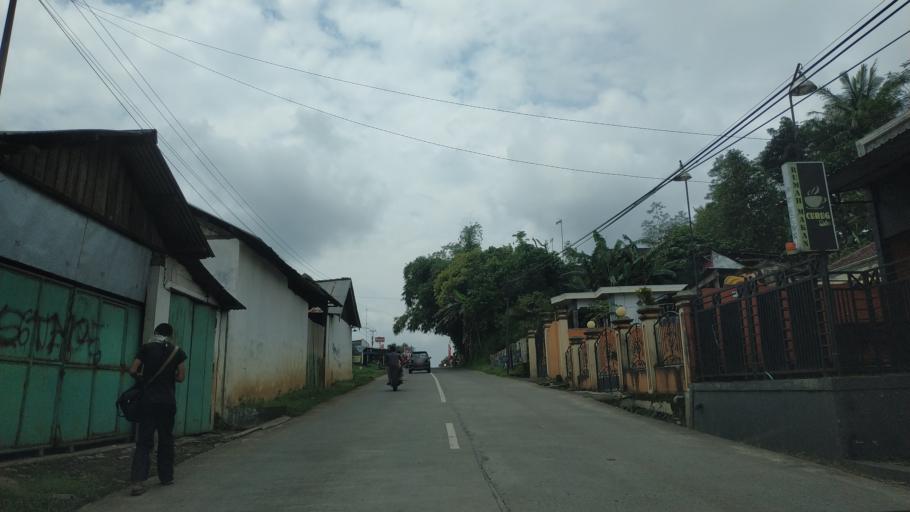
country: ID
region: Central Java
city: Weleri
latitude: -7.0960
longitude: 110.0586
